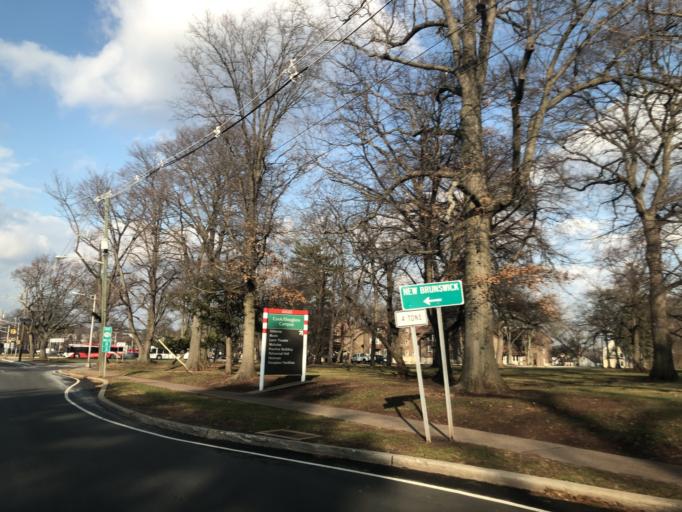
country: US
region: New Jersey
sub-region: Middlesex County
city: Highland Park
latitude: 40.4840
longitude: -74.4326
